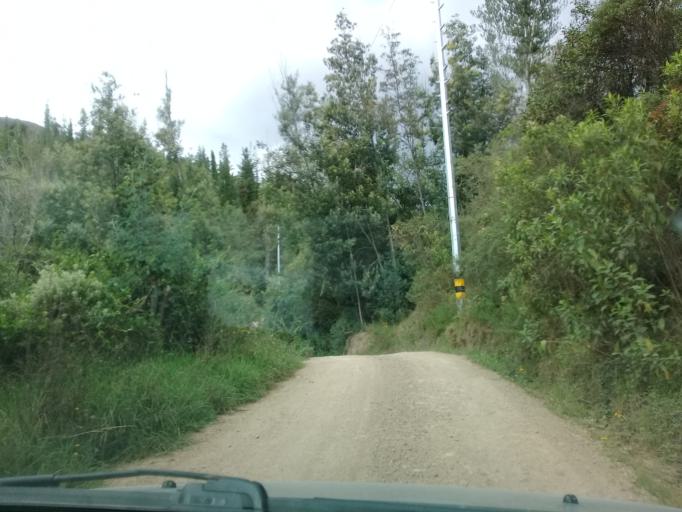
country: CO
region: Cundinamarca
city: Cucunuba
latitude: 5.2761
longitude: -73.7526
